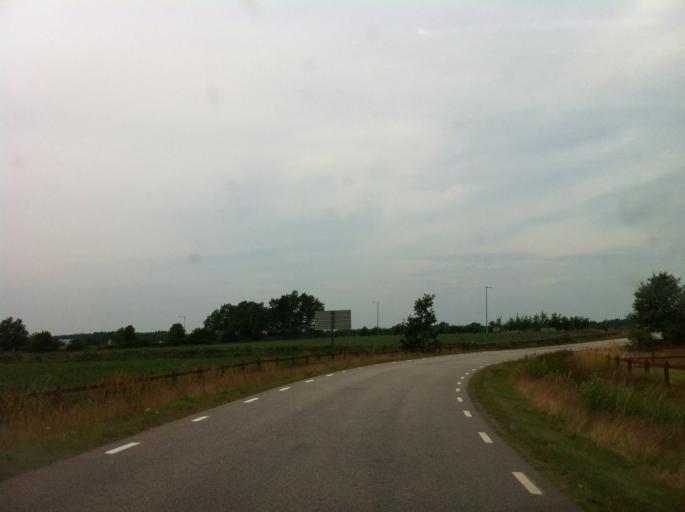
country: SE
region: Kalmar
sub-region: Torsas Kommun
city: Torsas
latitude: 56.3215
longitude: 16.0362
